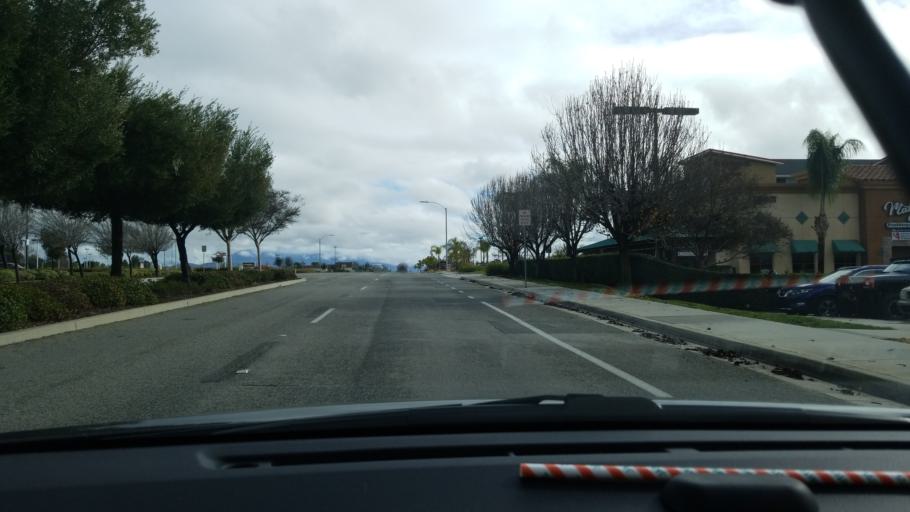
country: US
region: California
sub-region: Riverside County
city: Murrieta
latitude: 33.5516
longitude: -117.1944
